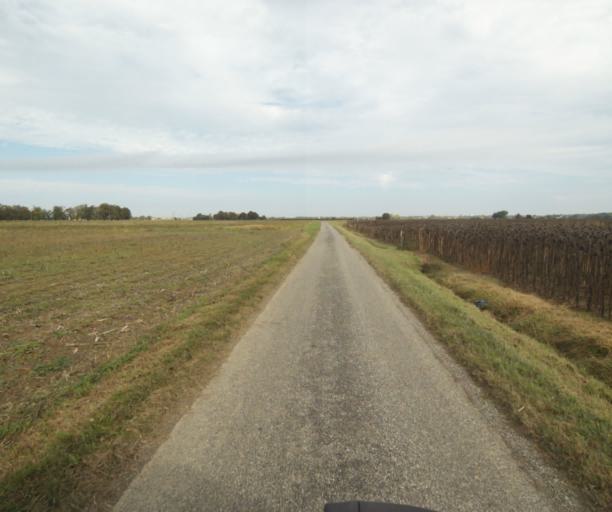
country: FR
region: Midi-Pyrenees
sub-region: Departement du Tarn-et-Garonne
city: Finhan
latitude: 43.9254
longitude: 1.2251
